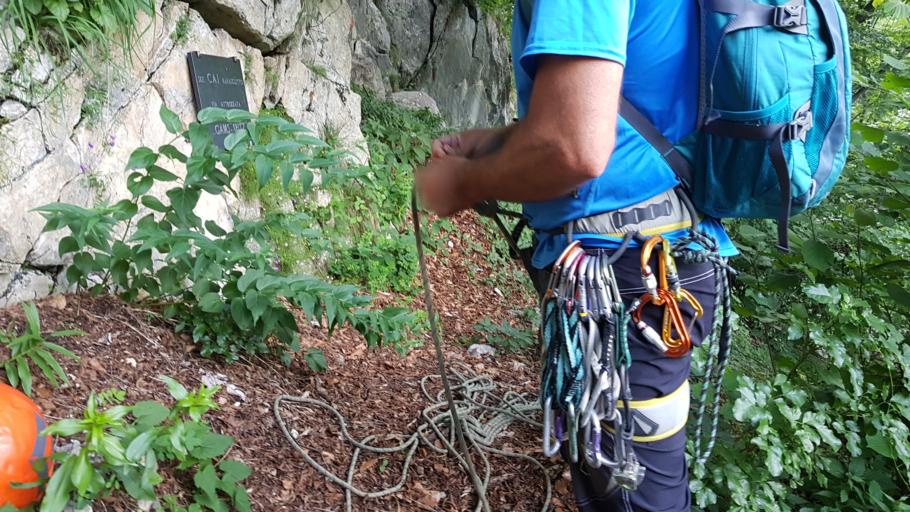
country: IT
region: Friuli Venezia Giulia
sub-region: Provincia di Udine
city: Paluzza
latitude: 46.5888
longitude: 12.9966
